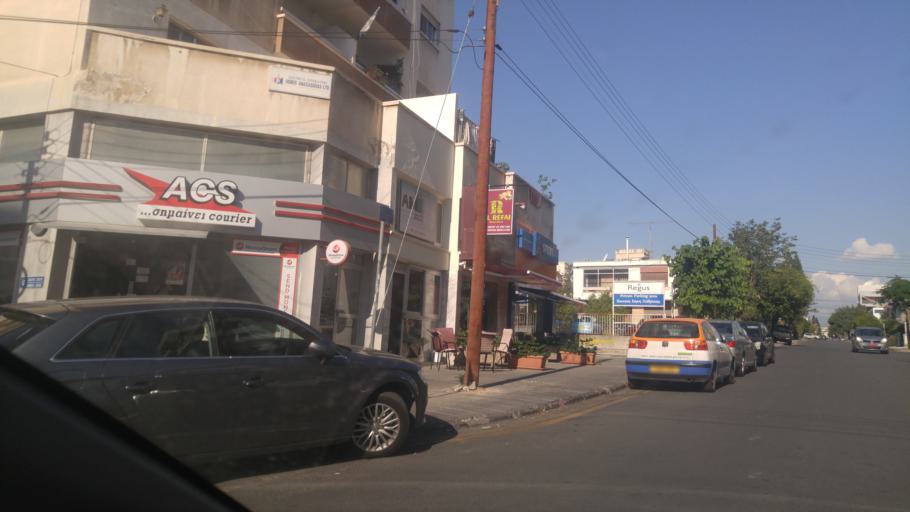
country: CY
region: Limassol
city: Limassol
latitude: 34.6873
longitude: 33.0534
